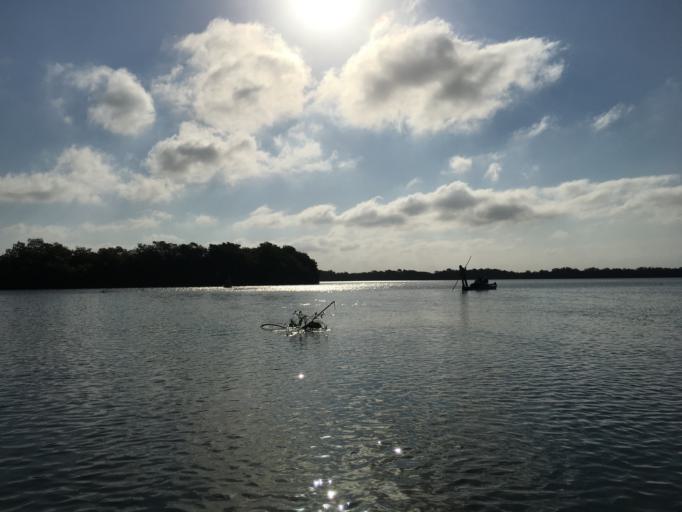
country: CO
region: Bolivar
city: Cartagena
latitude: 10.4853
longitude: -75.4833
